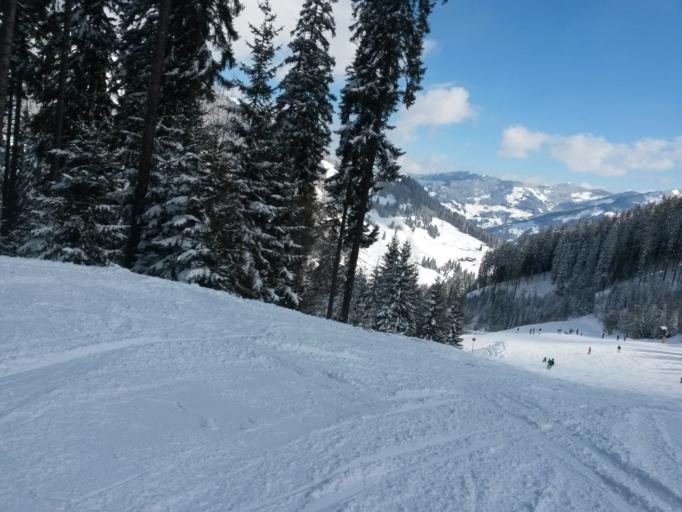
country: AT
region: Salzburg
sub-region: Politischer Bezirk Sankt Johann im Pongau
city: Dorfgastein
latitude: 47.2394
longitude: 13.1703
